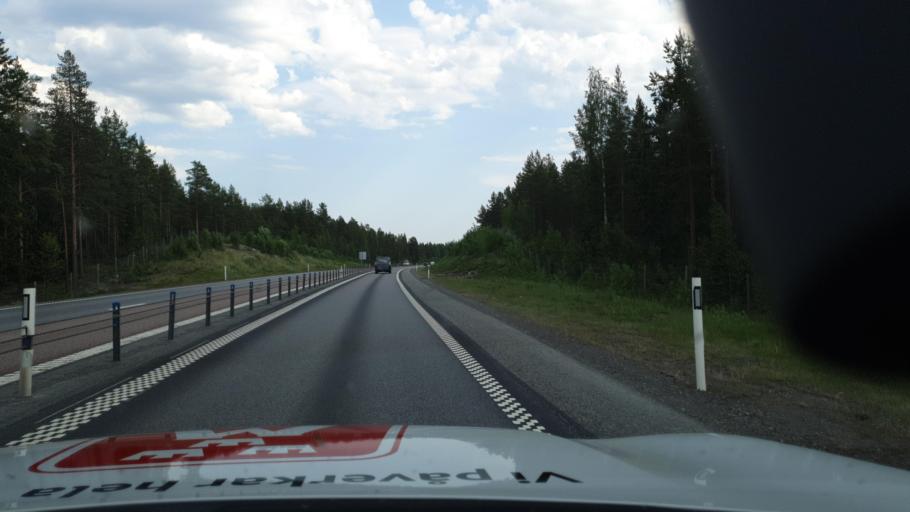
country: SE
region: Vaesterbotten
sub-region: Skelleftea Kommun
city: Burea
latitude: 64.6396
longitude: 21.1649
